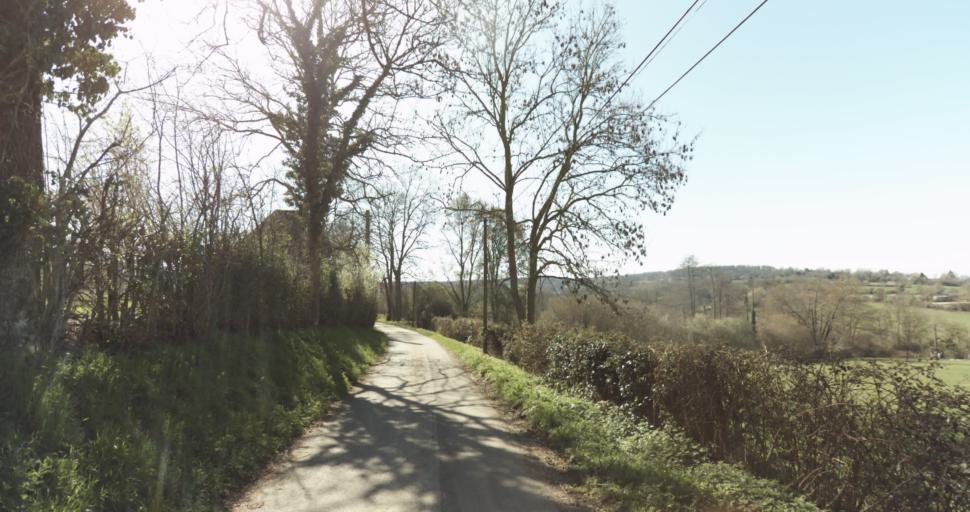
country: FR
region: Lower Normandy
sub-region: Departement du Calvados
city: Livarot
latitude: 48.9940
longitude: 0.0745
